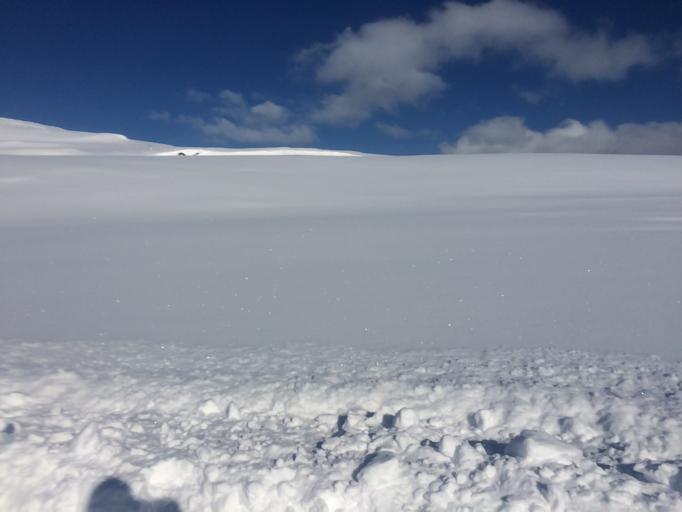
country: NO
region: Oppland
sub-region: Ringebu
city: Ringebu
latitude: 61.3665
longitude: 10.0759
